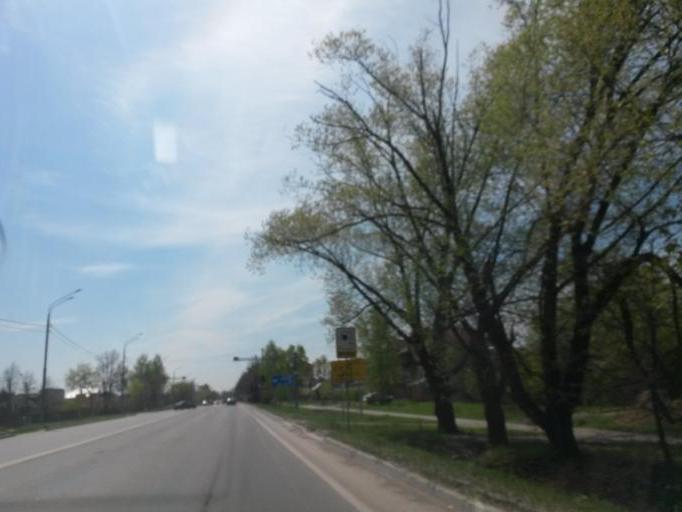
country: RU
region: Moskovskaya
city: Klimovsk
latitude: 55.3927
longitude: 37.5447
